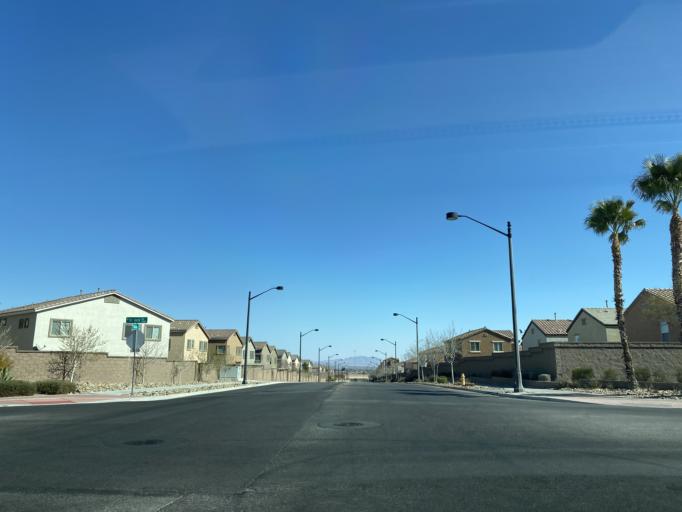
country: US
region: Nevada
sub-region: Clark County
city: Summerlin South
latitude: 36.3029
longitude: -115.2970
